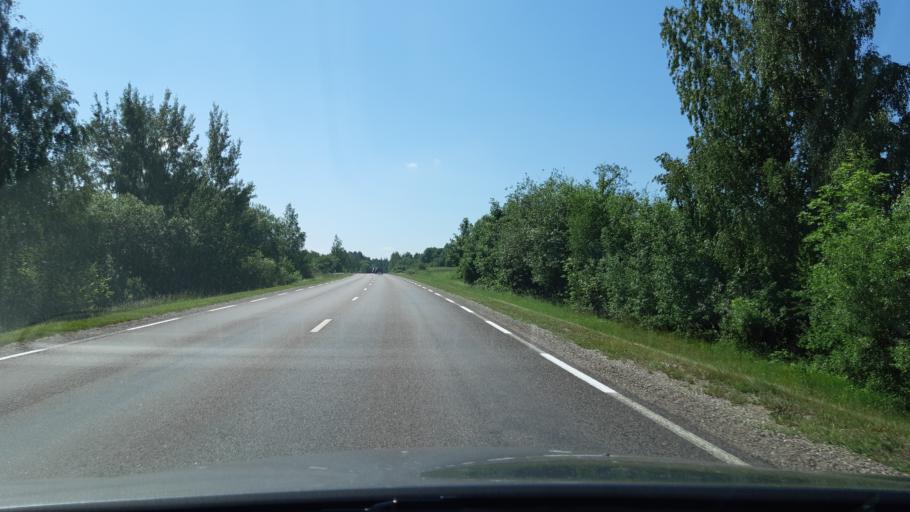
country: LT
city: Ziezmariai
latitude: 54.7847
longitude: 24.2809
